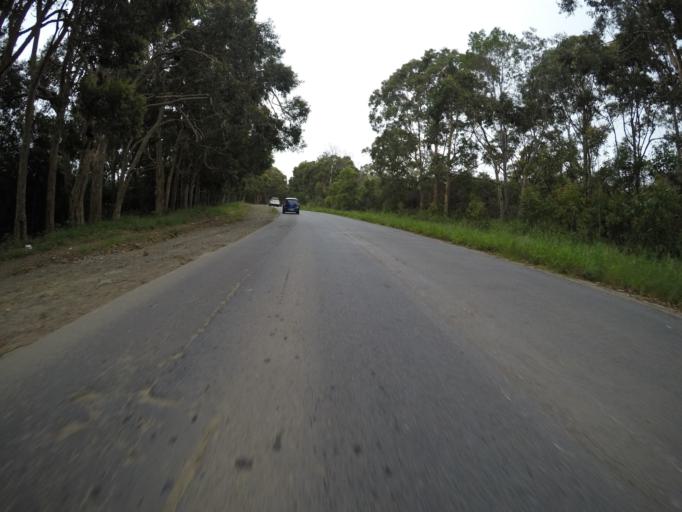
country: ZA
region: Eastern Cape
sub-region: Buffalo City Metropolitan Municipality
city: East London
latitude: -32.9378
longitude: 27.9429
